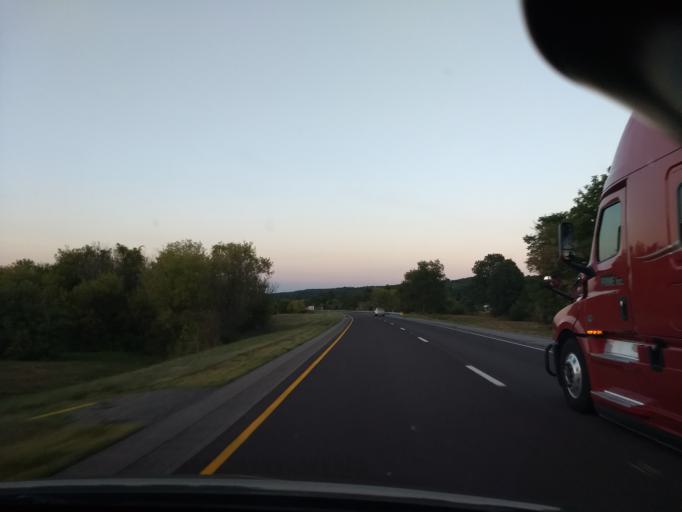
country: US
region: Pennsylvania
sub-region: Centre County
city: Zion
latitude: 40.9695
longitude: -77.6394
